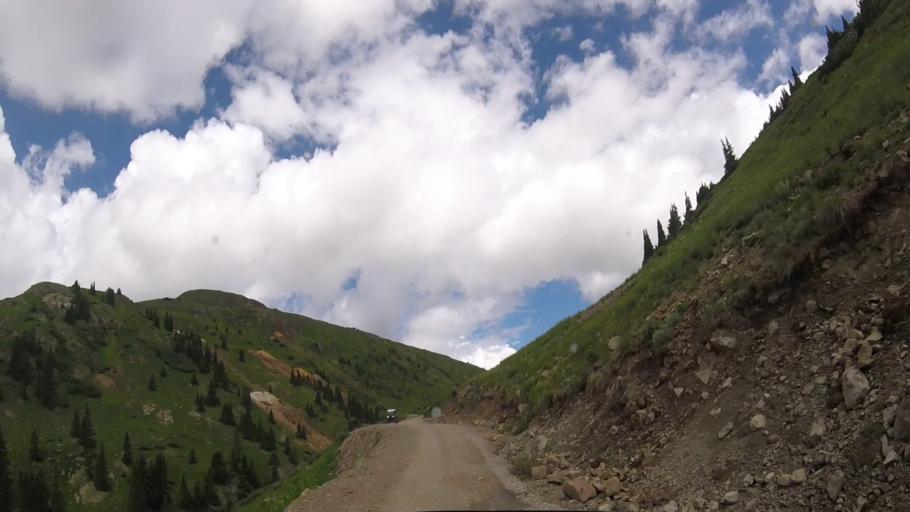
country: US
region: Colorado
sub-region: Ouray County
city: Ouray
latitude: 37.9361
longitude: -107.5704
